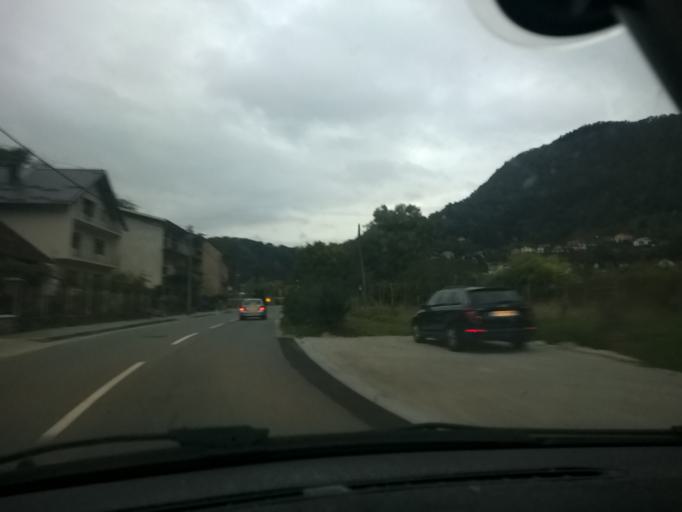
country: HR
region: Krapinsko-Zagorska
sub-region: Grad Krapina
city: Krapina
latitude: 46.1780
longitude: 15.8614
